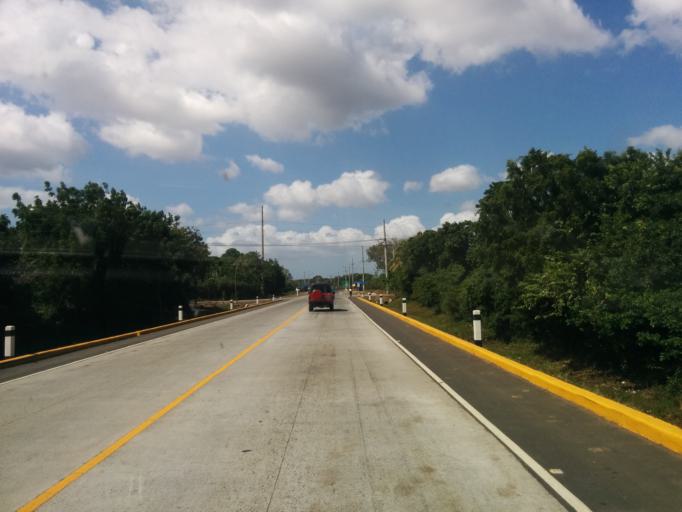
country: NI
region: Masaya
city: Masaya
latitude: 11.9941
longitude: -86.0783
